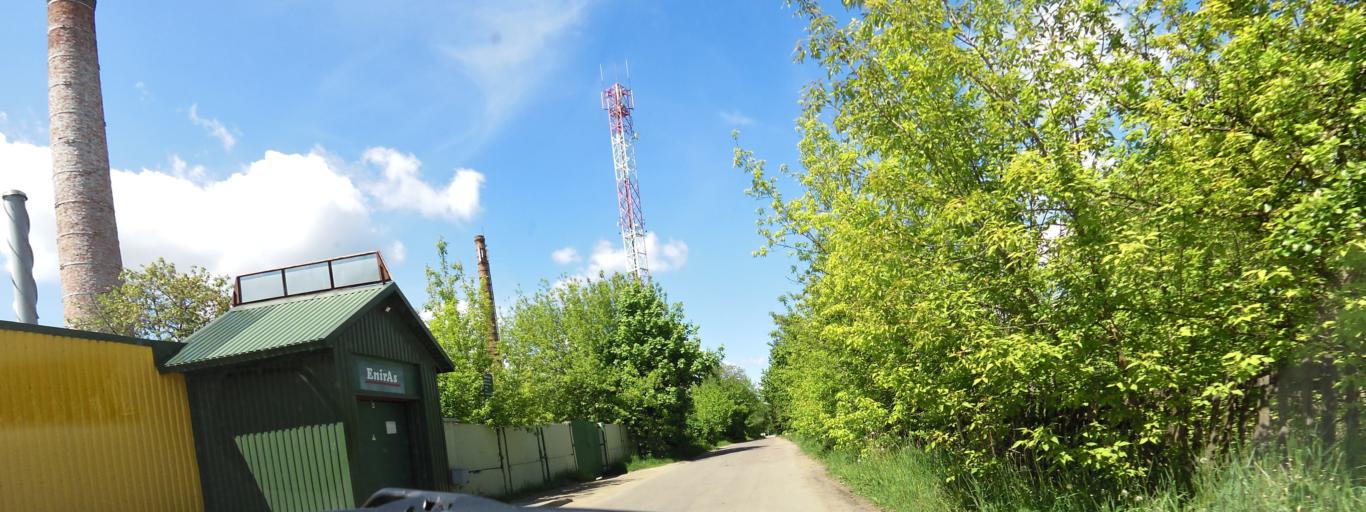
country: LT
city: Lentvaris
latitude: 54.6427
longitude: 25.0585
